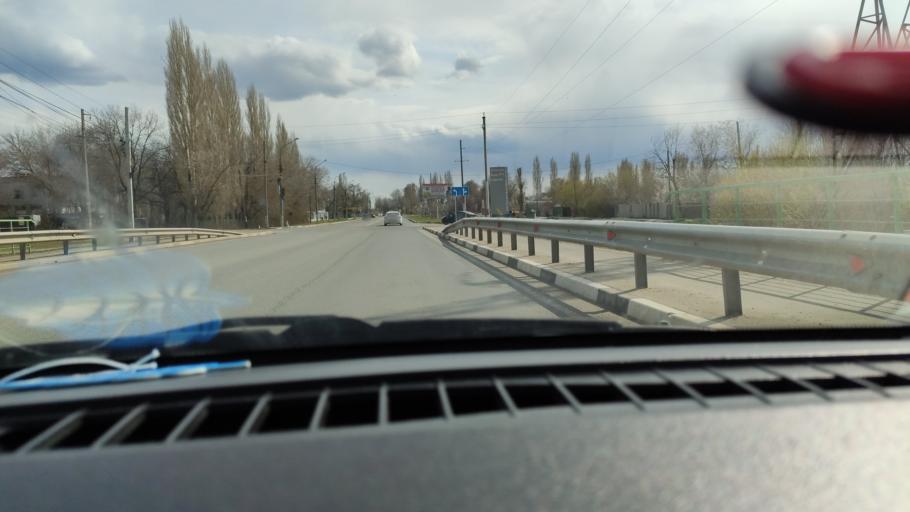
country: RU
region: Saratov
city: Privolzhskiy
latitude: 51.3923
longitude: 46.0345
